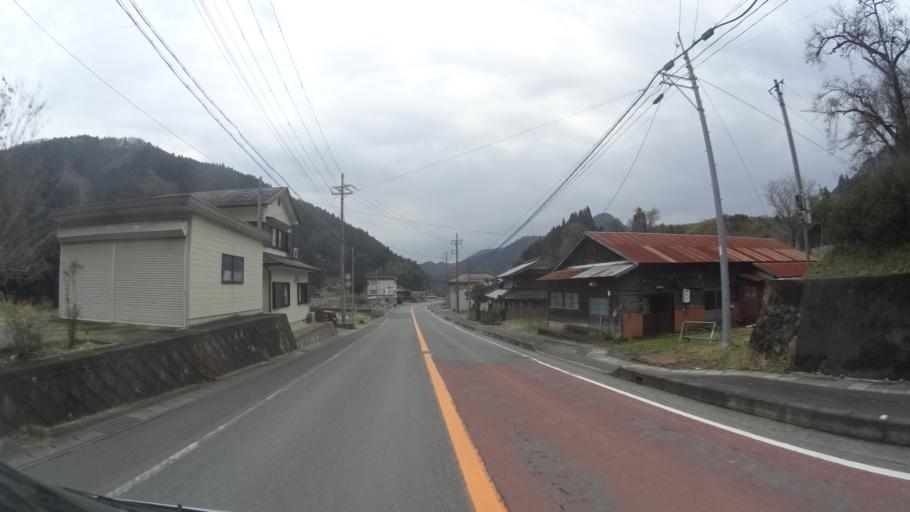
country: JP
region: Kyoto
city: Fukuchiyama
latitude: 35.3664
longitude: 135.0500
